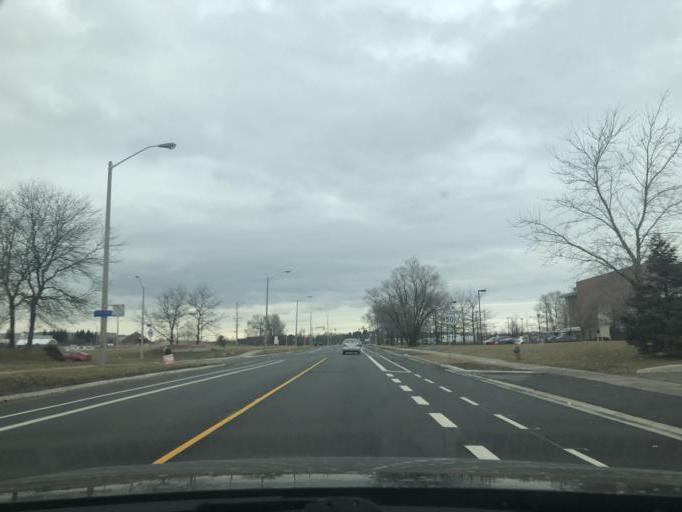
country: CA
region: Ontario
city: Scarborough
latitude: 43.8023
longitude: -79.1892
